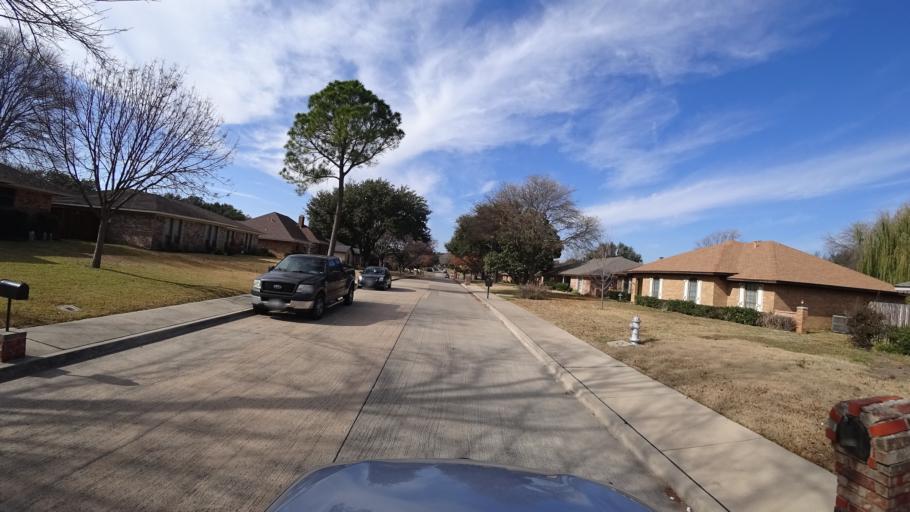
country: US
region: Texas
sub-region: Denton County
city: Lewisville
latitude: 33.0502
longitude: -97.0335
